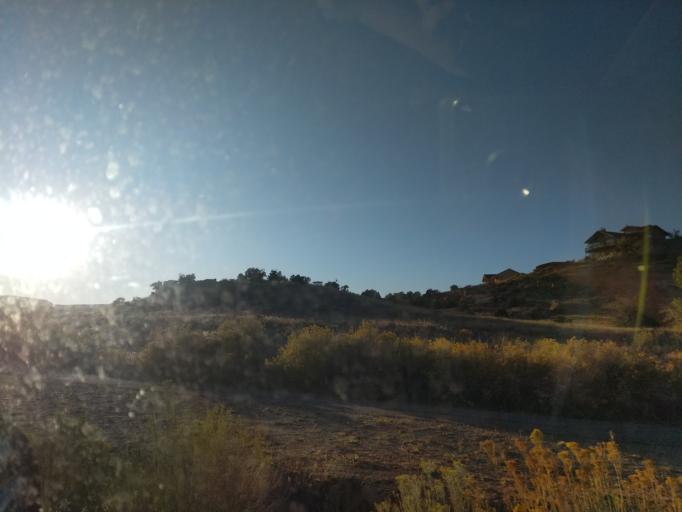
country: US
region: Colorado
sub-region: Mesa County
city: Redlands
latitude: 39.0579
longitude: -108.6123
